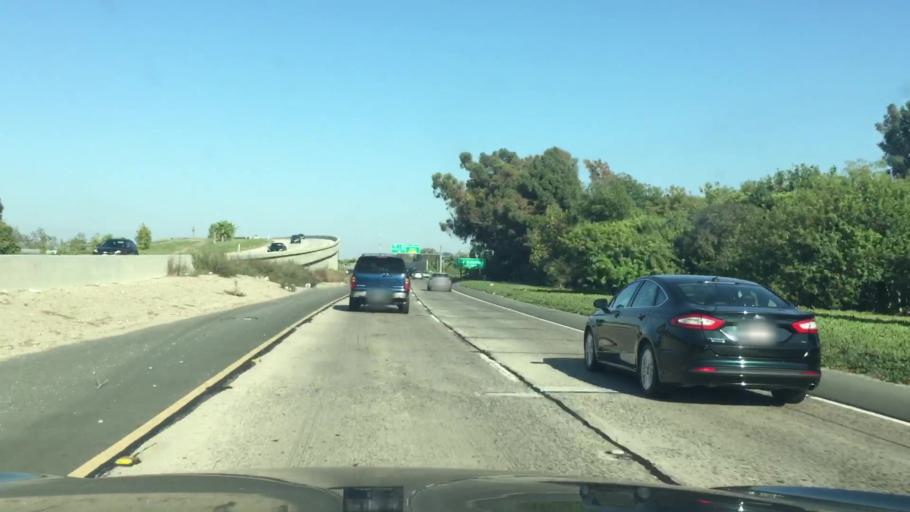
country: US
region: California
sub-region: Orange County
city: Rossmoor
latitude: 33.7743
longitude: -118.0905
